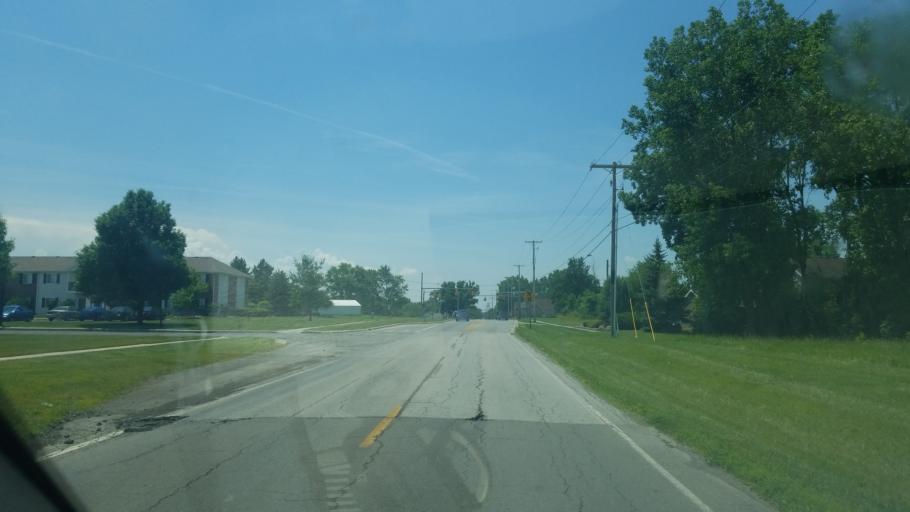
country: US
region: Ohio
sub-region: Hancock County
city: Findlay
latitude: 41.0671
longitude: -83.6308
